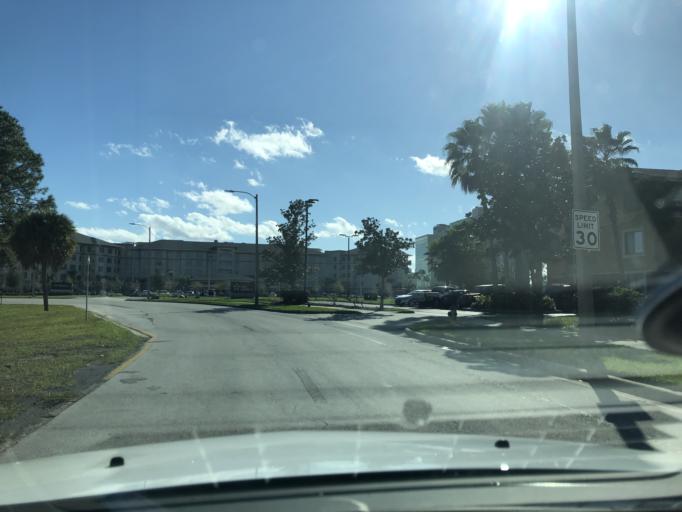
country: US
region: Florida
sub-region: Orange County
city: Tangelo Park
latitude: 28.4823
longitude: -81.4556
